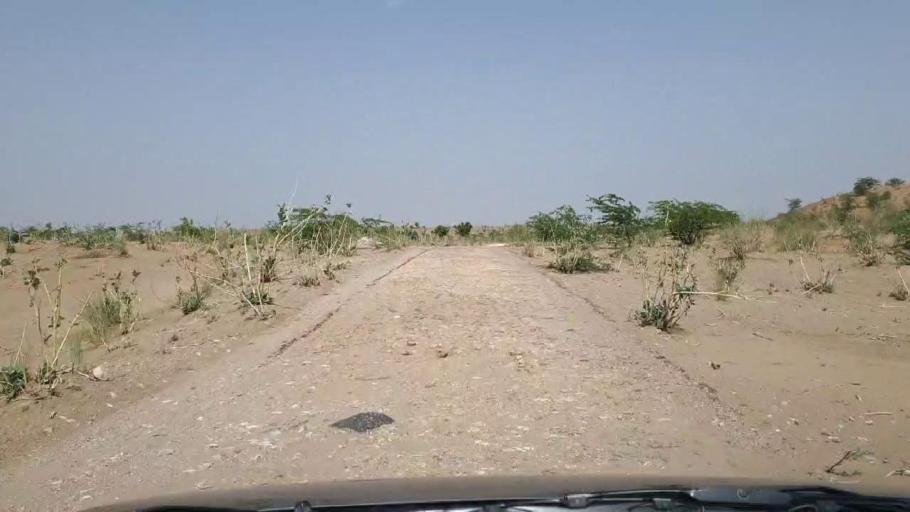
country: PK
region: Sindh
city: Chor
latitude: 25.4718
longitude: 70.5165
